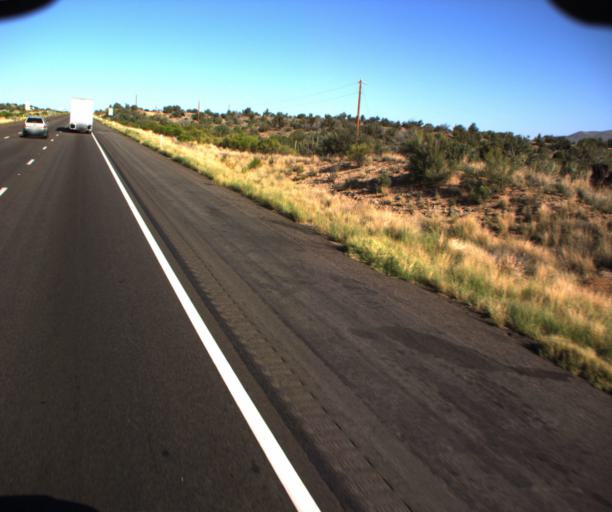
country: US
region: Arizona
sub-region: Mohave County
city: New Kingman-Butler
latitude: 35.1641
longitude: -113.7279
